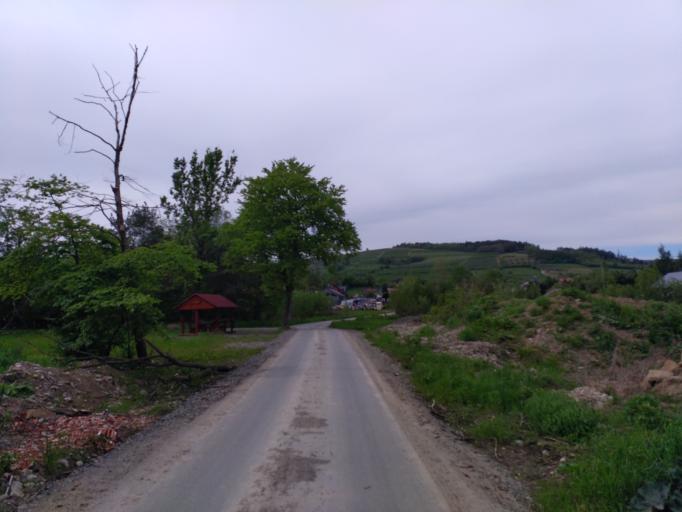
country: PL
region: Lesser Poland Voivodeship
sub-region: Powiat nowosadecki
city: Lacko
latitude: 49.5511
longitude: 20.4304
